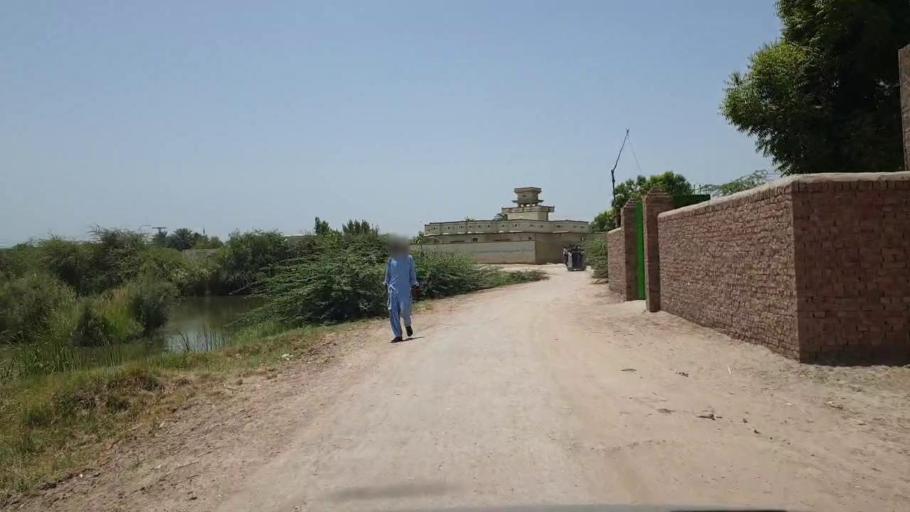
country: PK
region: Sindh
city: Sakrand
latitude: 26.1085
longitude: 68.3902
